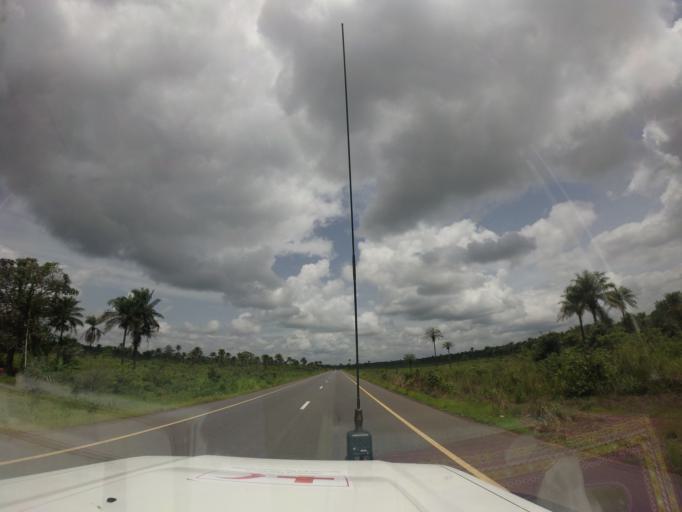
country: SL
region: Northern Province
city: Mange
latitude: 8.9507
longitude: -12.8626
